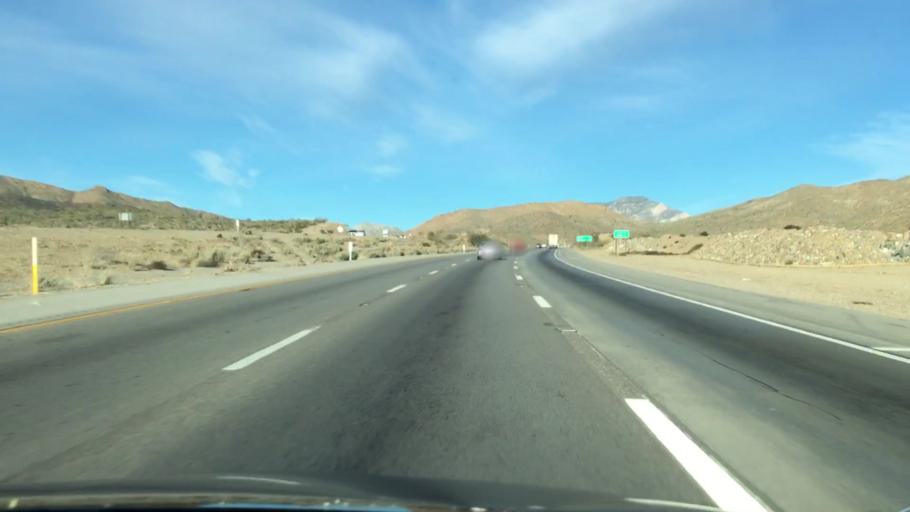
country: US
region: Nevada
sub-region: Clark County
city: Sandy Valley
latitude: 35.4628
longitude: -115.4781
